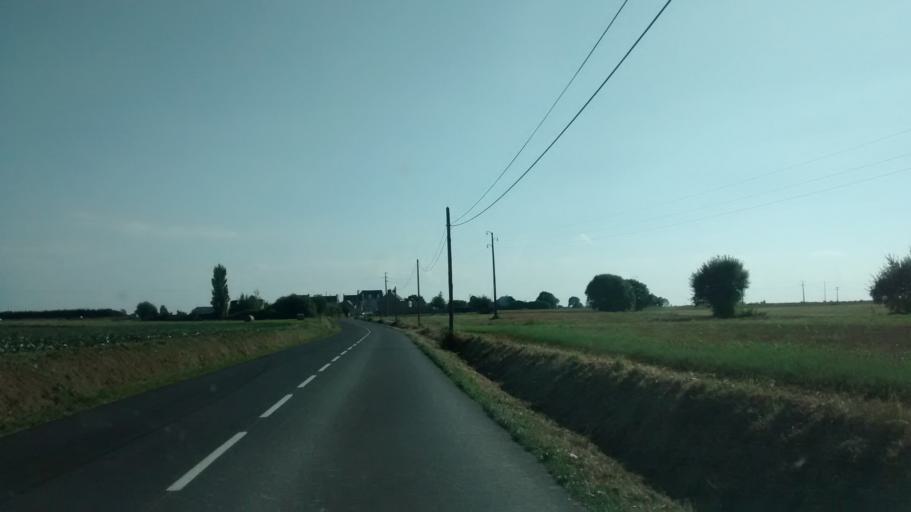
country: FR
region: Brittany
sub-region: Departement d'Ille-et-Vilaine
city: Saint-Meloir-des-Ondes
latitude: 48.6516
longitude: -1.9024
